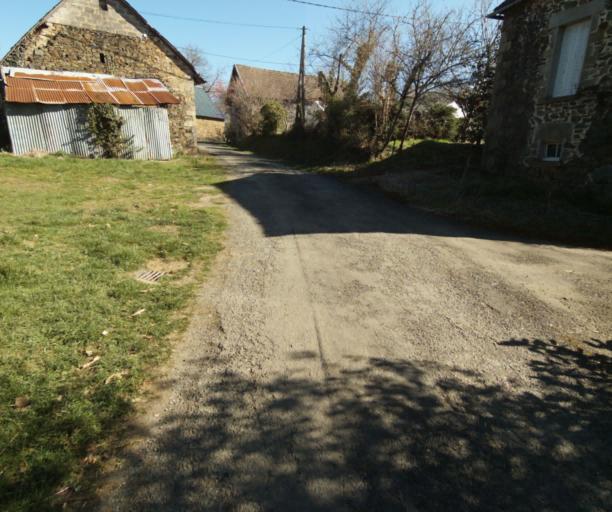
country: FR
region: Limousin
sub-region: Departement de la Correze
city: Seilhac
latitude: 45.3858
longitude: 1.7509
